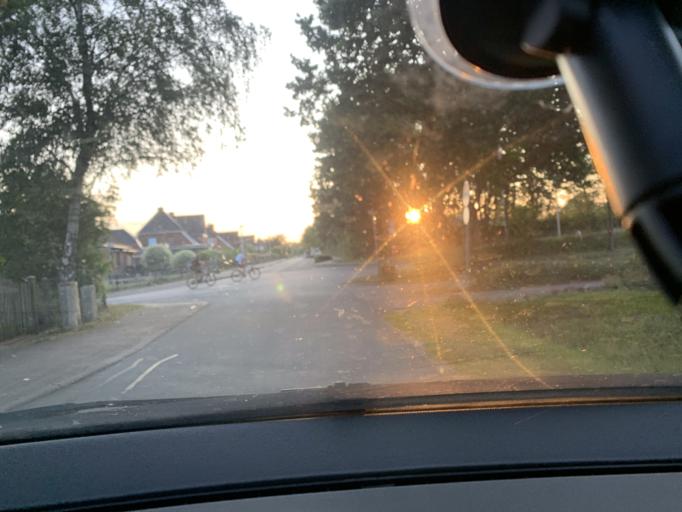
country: DE
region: Schleswig-Holstein
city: Mildstedt
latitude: 54.4670
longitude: 9.1001
